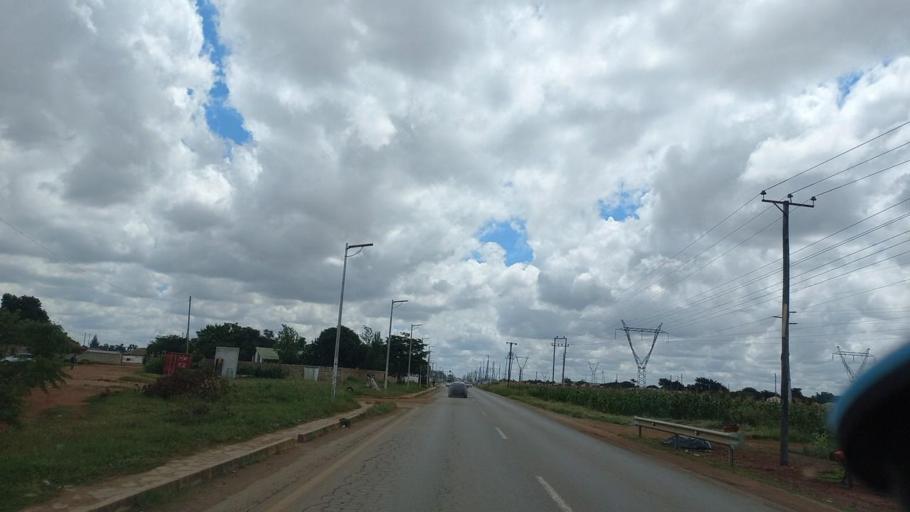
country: ZM
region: Lusaka
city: Lusaka
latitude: -15.4579
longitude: 28.3309
